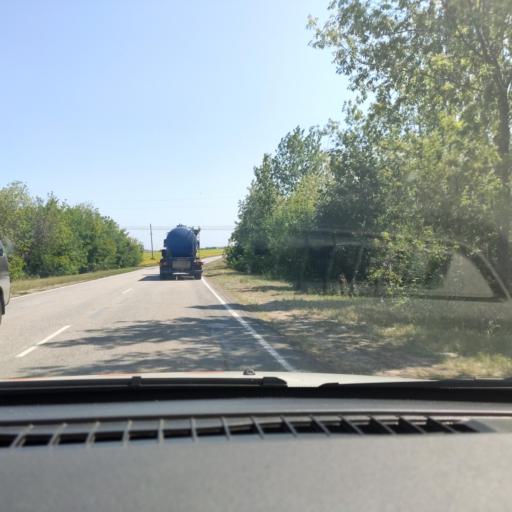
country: RU
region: Voronezj
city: Ostrogozhsk
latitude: 50.8125
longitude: 39.2700
